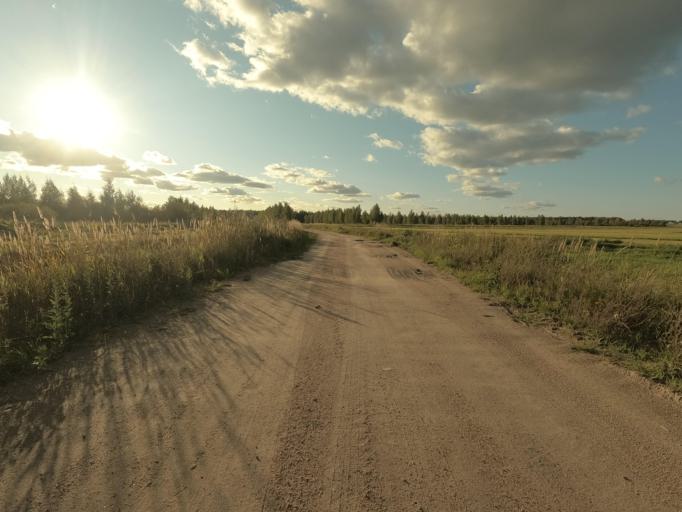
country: RU
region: Leningrad
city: Imeni Sverdlova
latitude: 59.8598
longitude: 30.7344
